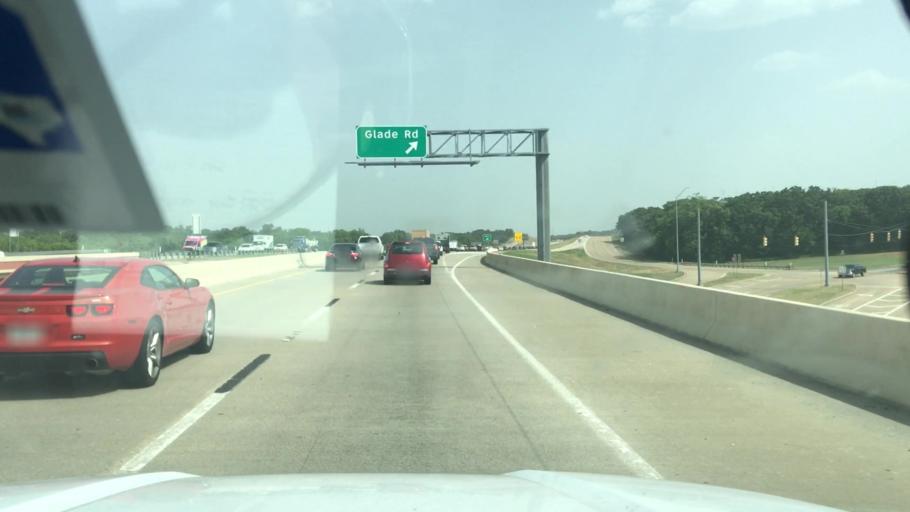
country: US
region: Texas
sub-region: Tarrant County
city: Grapevine
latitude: 32.8919
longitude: -97.0824
